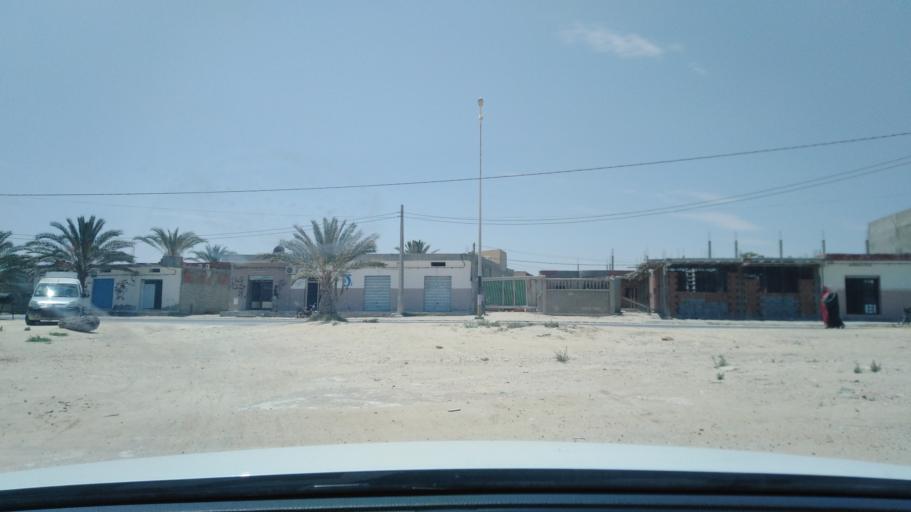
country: TN
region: Qabis
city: Gabes
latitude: 33.9507
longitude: 10.0695
